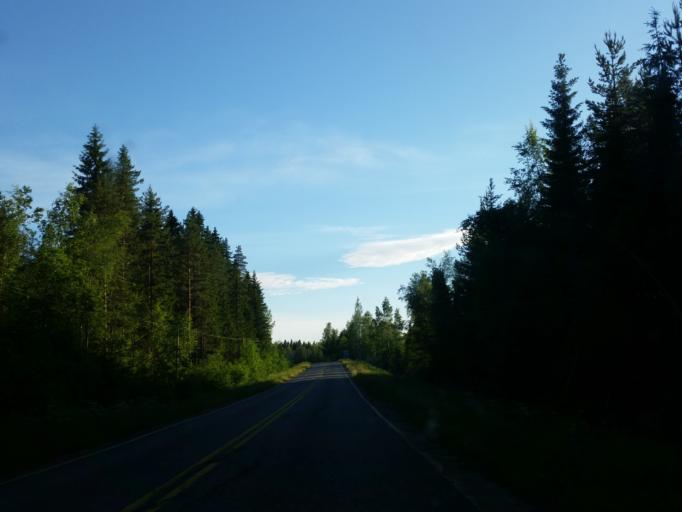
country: FI
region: Northern Savo
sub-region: Sisae-Savo
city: Tervo
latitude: 63.0379
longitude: 26.7597
